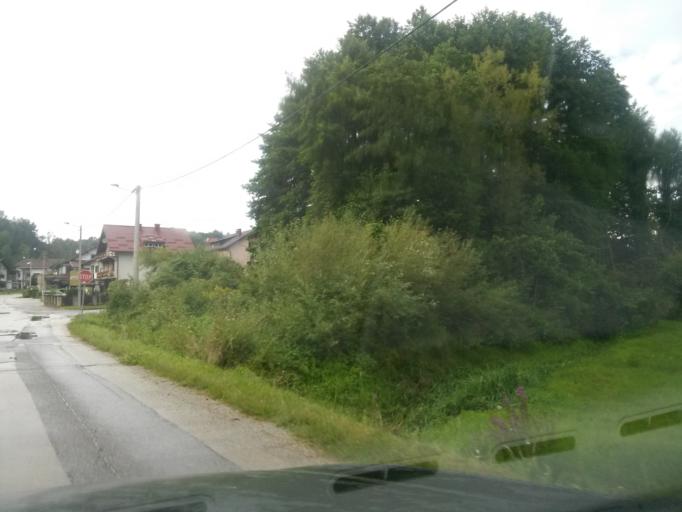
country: HR
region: Sisacko-Moslavacka
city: Gvozd
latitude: 45.2999
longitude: 15.9691
